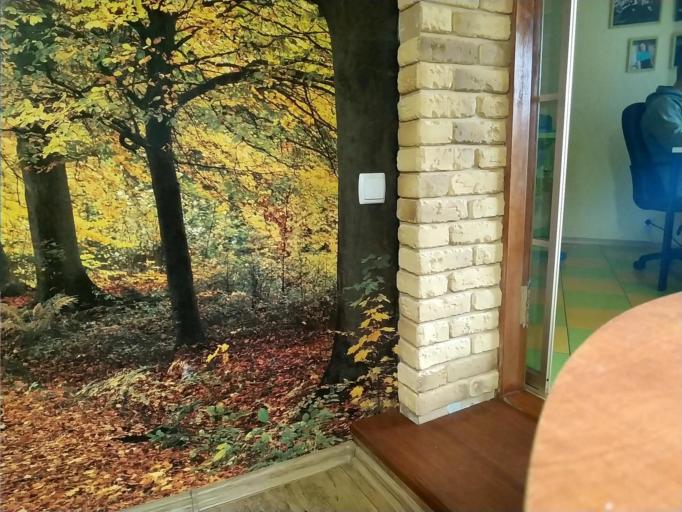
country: RU
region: Smolensk
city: Dorogobuzh
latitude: 54.9779
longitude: 33.2761
